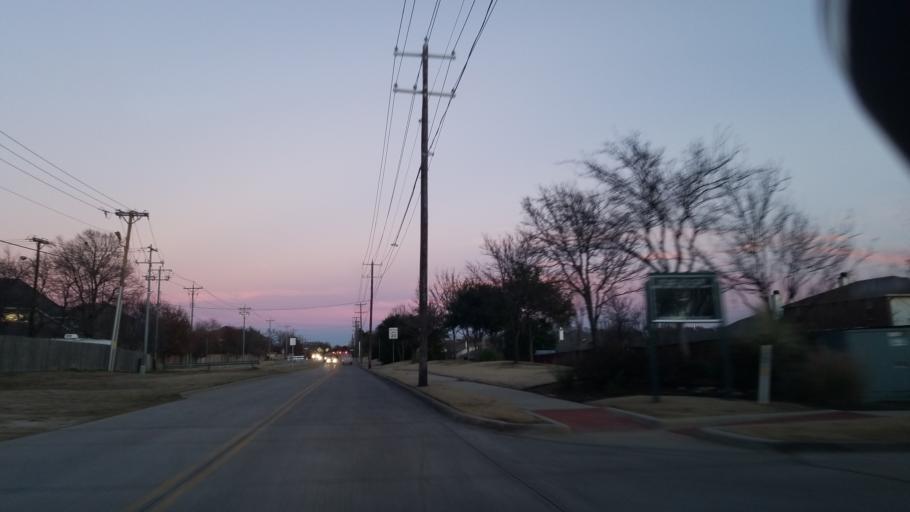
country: US
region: Texas
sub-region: Denton County
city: Corinth
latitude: 33.1583
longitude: -97.0973
